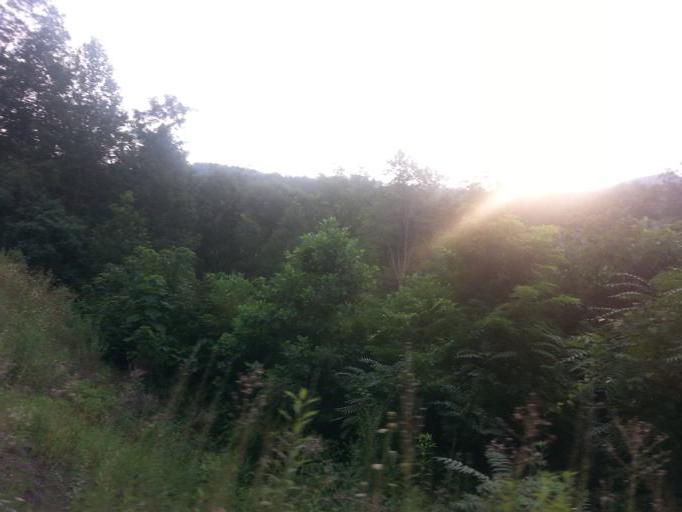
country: US
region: Tennessee
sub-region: Anderson County
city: Clinton
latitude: 36.1361
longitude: -84.2371
